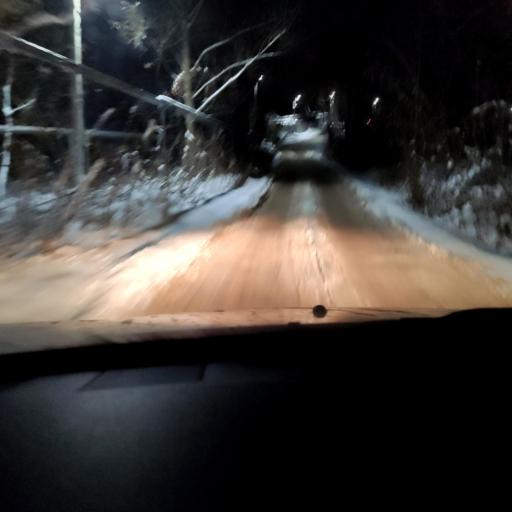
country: RU
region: Samara
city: Petra-Dubrava
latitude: 53.3187
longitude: 50.2928
